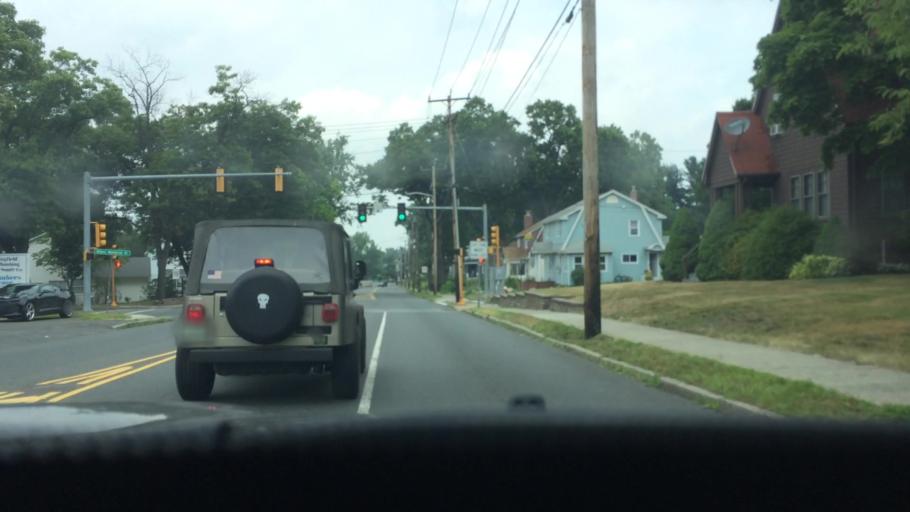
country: US
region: Massachusetts
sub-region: Hampden County
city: Chicopee
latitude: 42.1405
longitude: -72.5817
